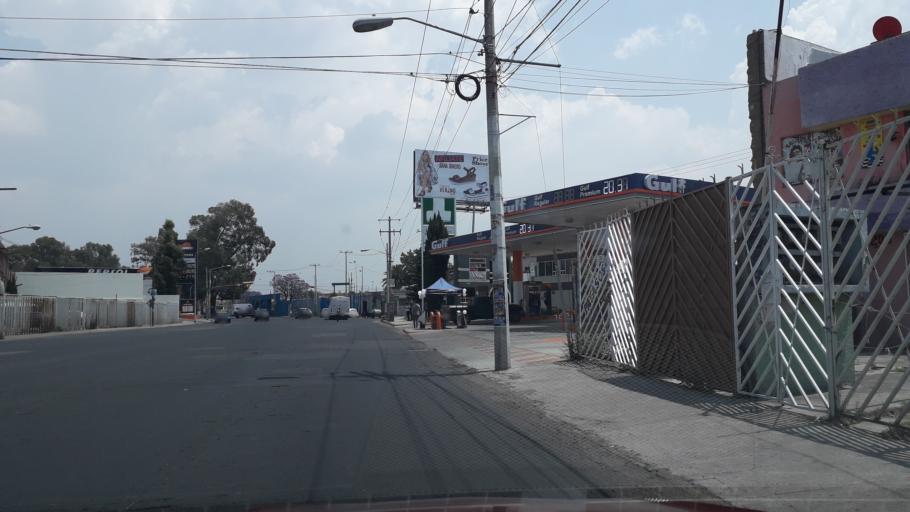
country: MX
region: Puebla
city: Puebla
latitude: 19.0469
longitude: -98.1730
